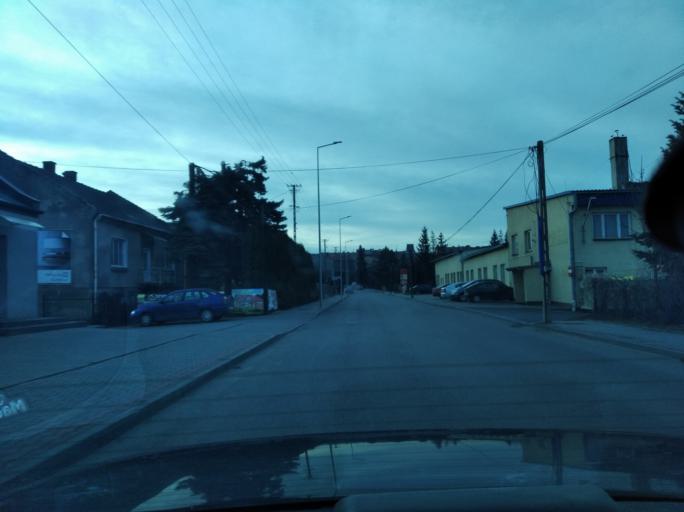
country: PL
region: Subcarpathian Voivodeship
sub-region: Powiat ropczycko-sedziszowski
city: Sedziszow Malopolski
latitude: 50.0735
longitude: 21.6996
